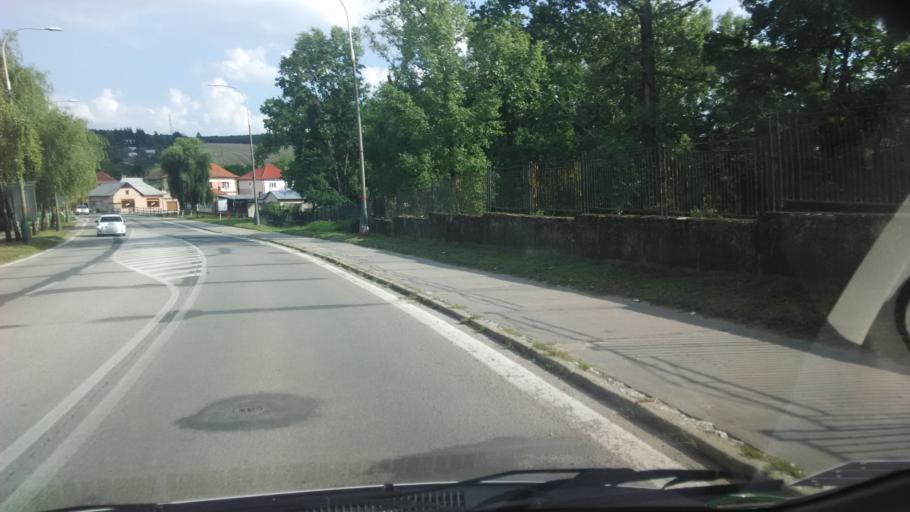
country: SK
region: Nitriansky
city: Banovce nad Bebravou
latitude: 48.7183
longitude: 18.2607
